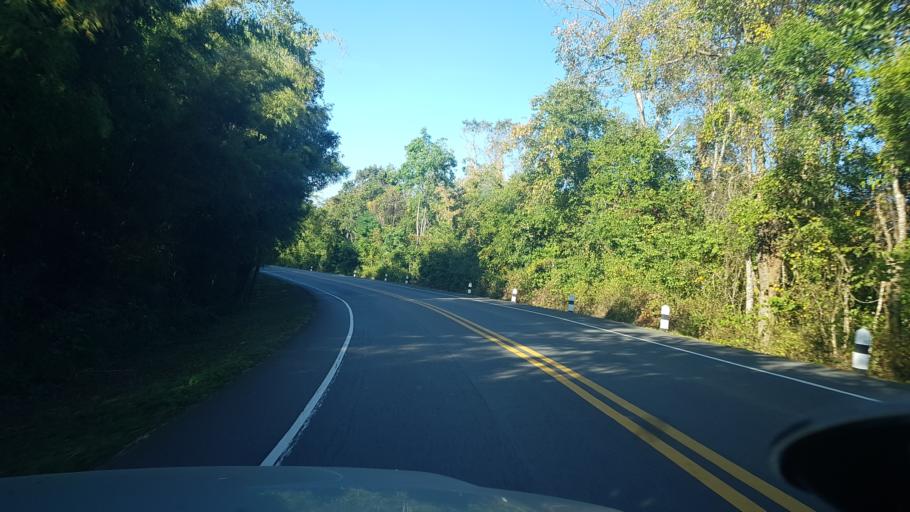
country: TH
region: Phetchabun
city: Nam Nao
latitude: 16.7615
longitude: 101.4735
